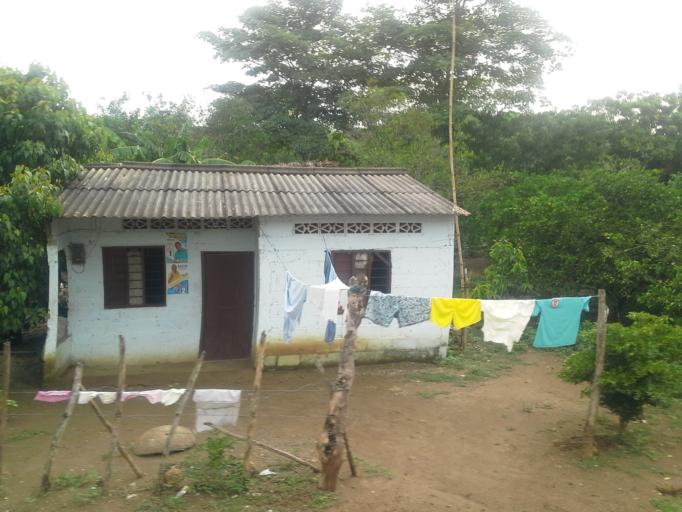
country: CO
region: Sucre
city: Coloso
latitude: 9.4593
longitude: -75.3683
